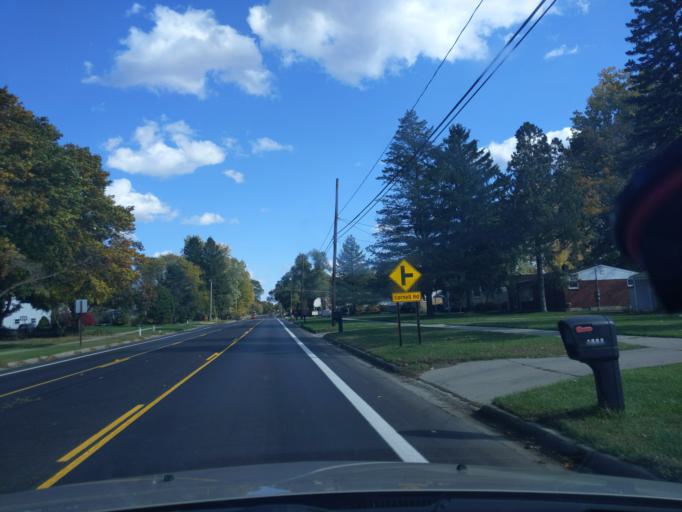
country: US
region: Michigan
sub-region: Ingham County
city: Haslett
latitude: 42.7467
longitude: -84.3950
